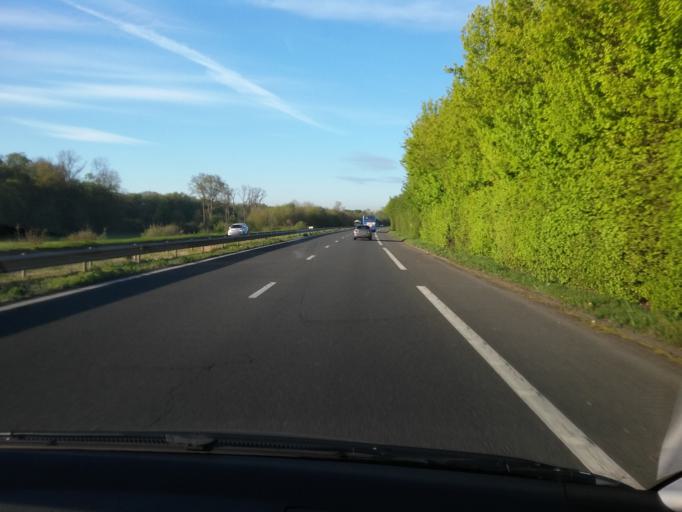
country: FR
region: Picardie
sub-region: Departement de l'Oise
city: Jaux
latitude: 49.3736
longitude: 2.7800
